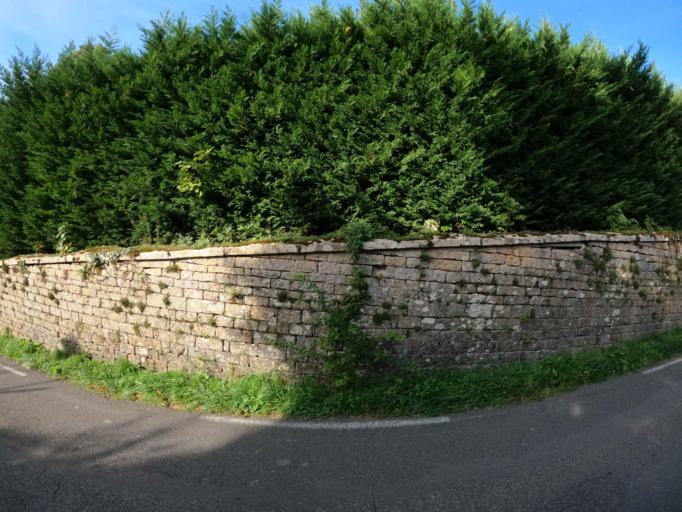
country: FR
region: Franche-Comte
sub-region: Departement du Jura
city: Montmorot
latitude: 46.6830
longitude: 5.5375
